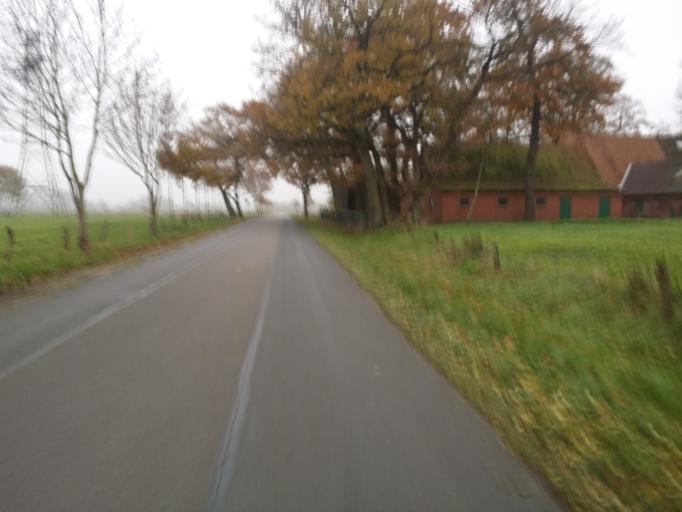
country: DE
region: Lower Saxony
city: Delmenhorst
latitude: 53.0189
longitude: 8.6232
